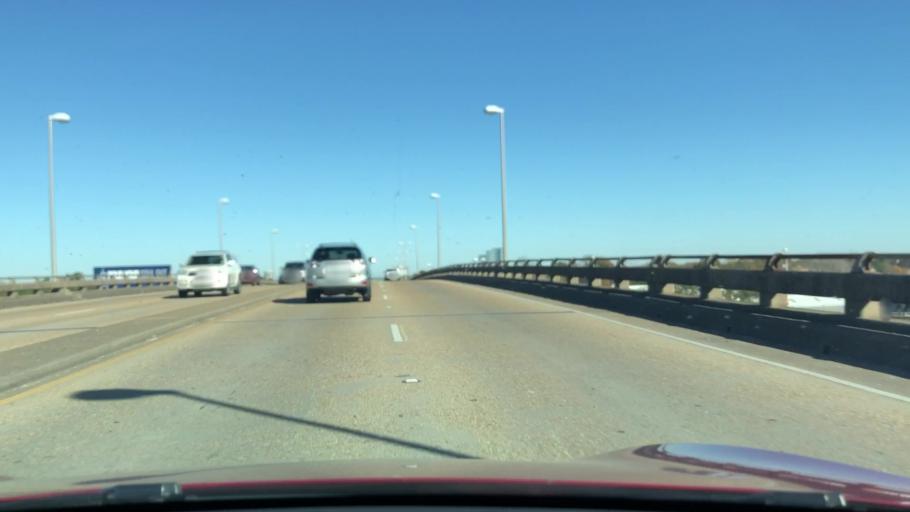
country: US
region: Louisiana
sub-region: Jefferson Parish
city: Metairie Terrace
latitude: 29.9742
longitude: -90.1563
